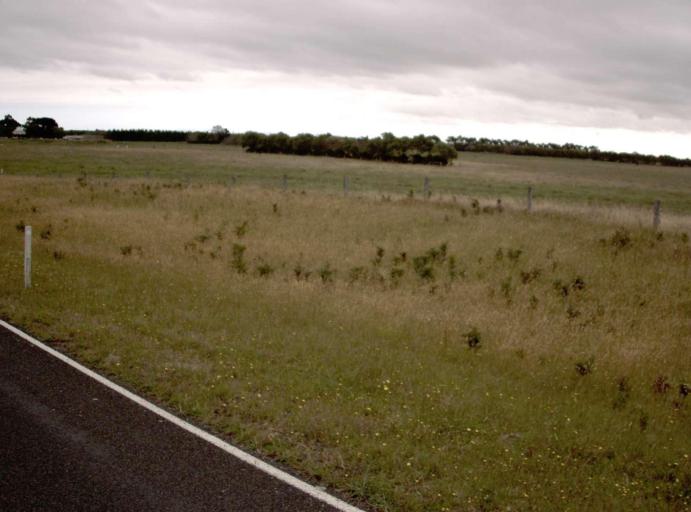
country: AU
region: Victoria
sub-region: Wellington
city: Sale
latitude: -38.5422
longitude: 146.8876
